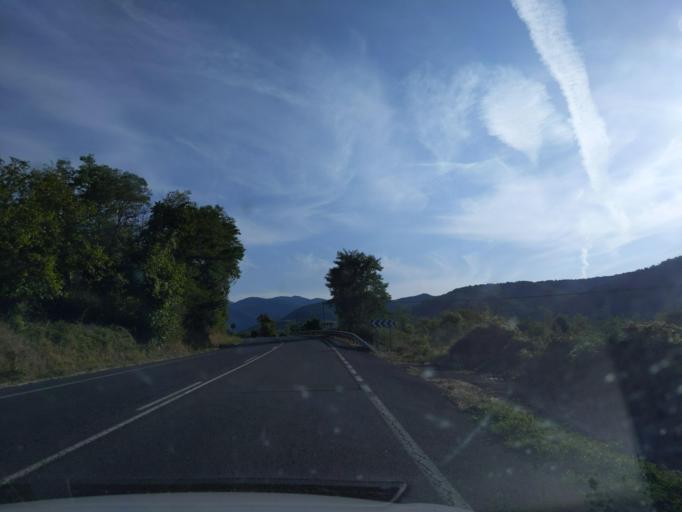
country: ES
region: La Rioja
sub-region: Provincia de La Rioja
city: Ojacastro
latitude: 42.3649
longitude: -2.9844
